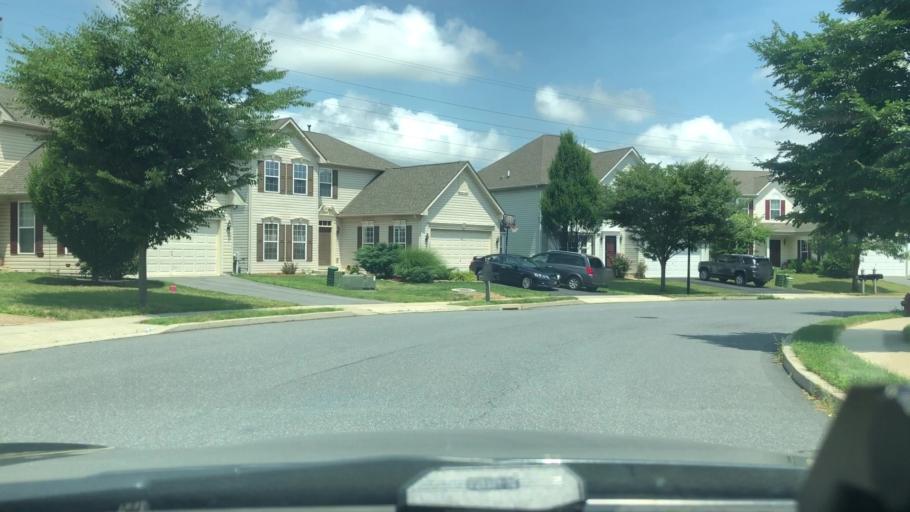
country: US
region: Pennsylvania
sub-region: Northampton County
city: Bethlehem
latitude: 40.6529
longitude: -75.4020
